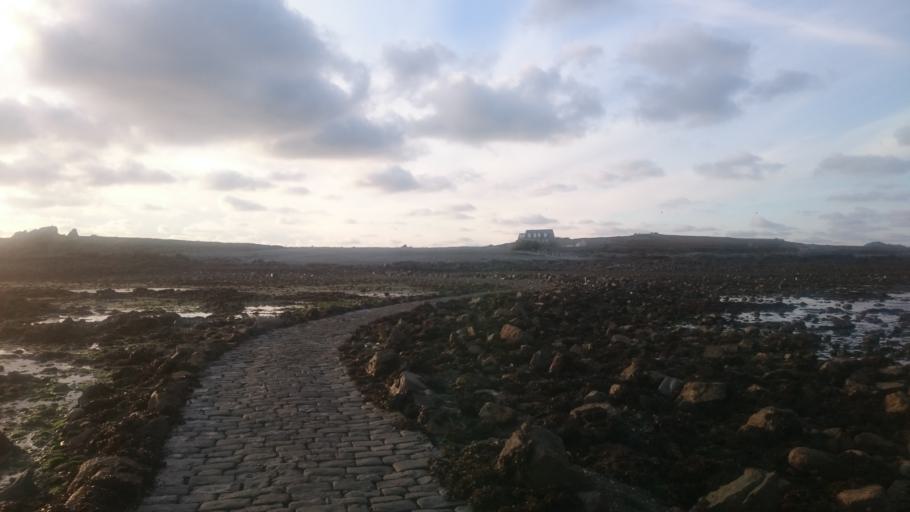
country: GG
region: St Peter Port
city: Saint Peter Port
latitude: 49.4585
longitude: -2.6611
